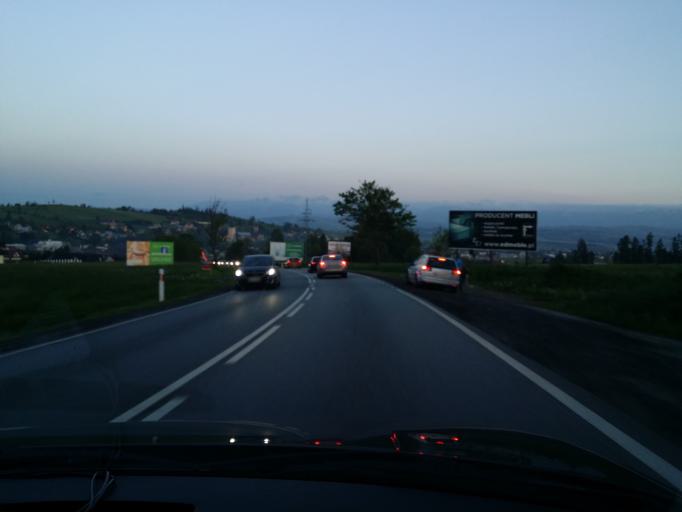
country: PL
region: Lesser Poland Voivodeship
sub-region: Powiat nowotarski
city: Klikuszowa
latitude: 49.5252
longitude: 19.9790
